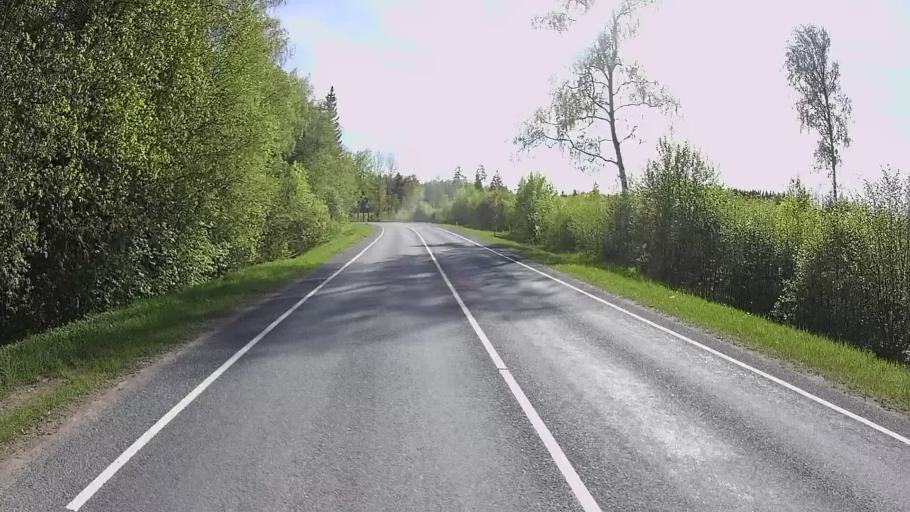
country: EE
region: Vorumaa
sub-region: Antsla vald
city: Vana-Antsla
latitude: 57.9717
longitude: 26.4633
